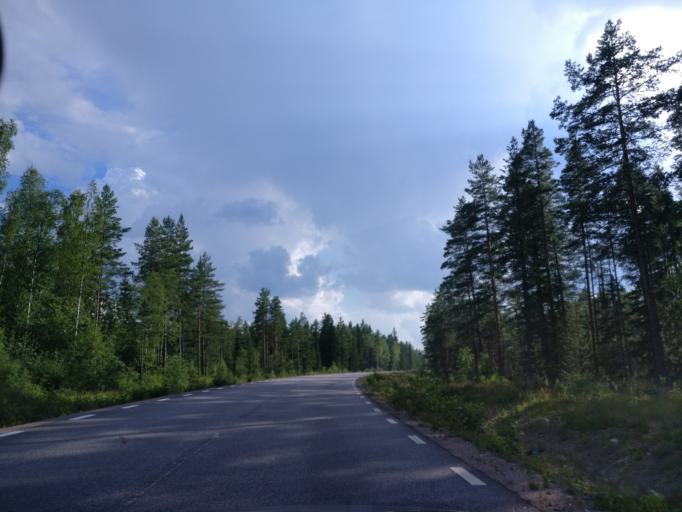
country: SE
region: Dalarna
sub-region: Ludvika Kommun
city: Abborrberget
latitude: 60.1844
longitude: 14.7191
